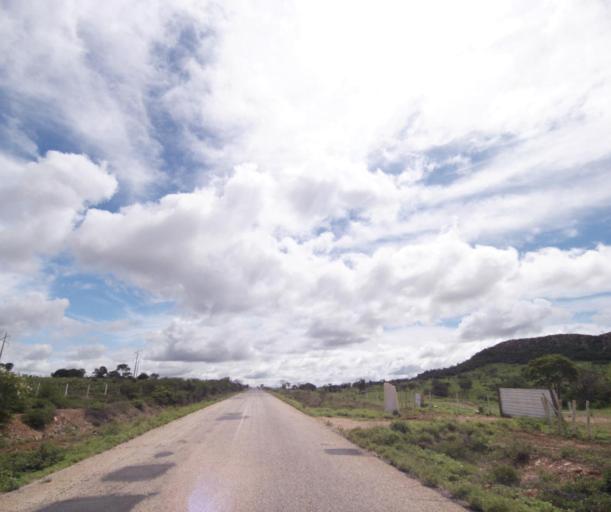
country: BR
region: Bahia
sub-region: Brumado
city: Brumado
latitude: -14.1570
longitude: -41.5206
